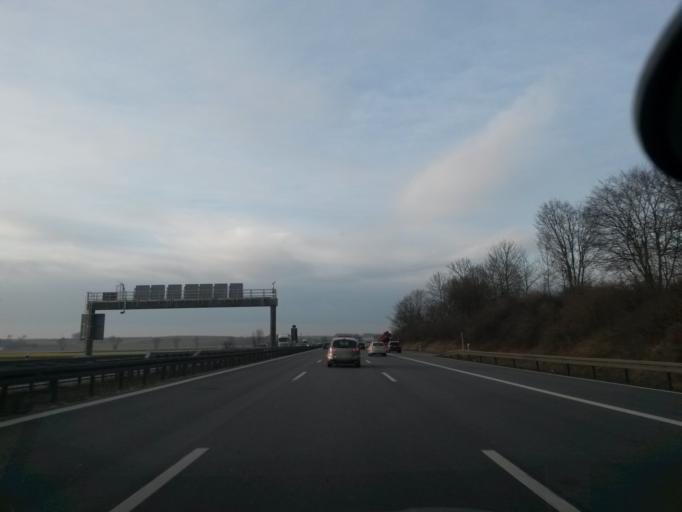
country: DE
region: Bavaria
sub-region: Upper Bavaria
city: Kranzberg
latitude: 48.3806
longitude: 11.5967
